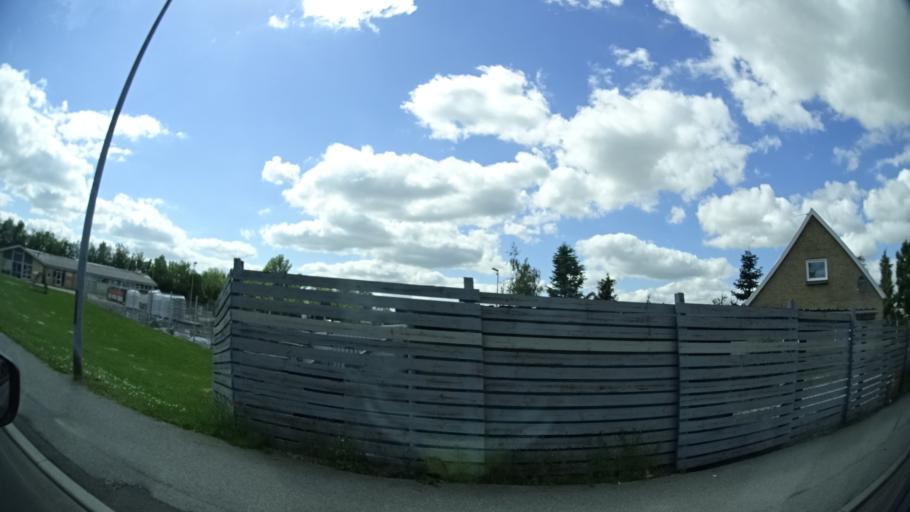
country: DK
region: Central Jutland
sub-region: Syddjurs Kommune
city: Ronde
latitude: 56.3018
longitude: 10.4653
